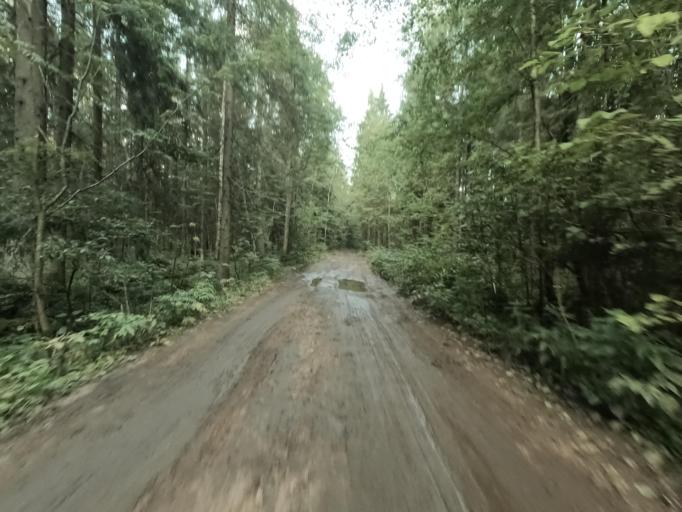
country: RU
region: Leningrad
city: Otradnoye
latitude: 59.8324
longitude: 30.7676
